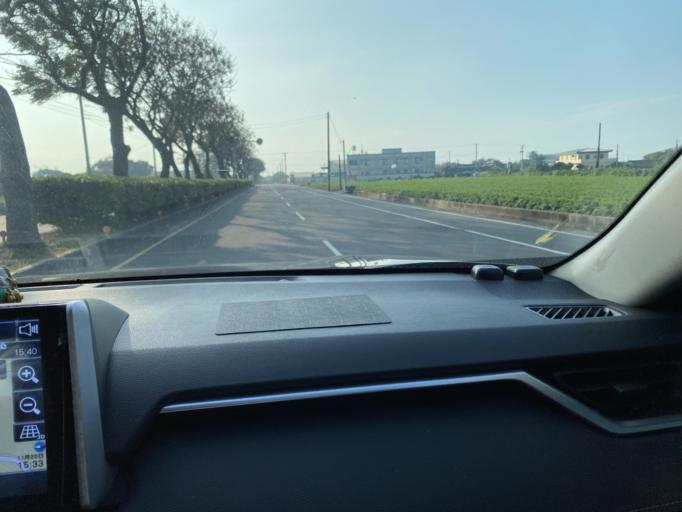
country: TW
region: Taiwan
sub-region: Changhua
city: Chang-hua
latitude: 23.9612
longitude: 120.3891
